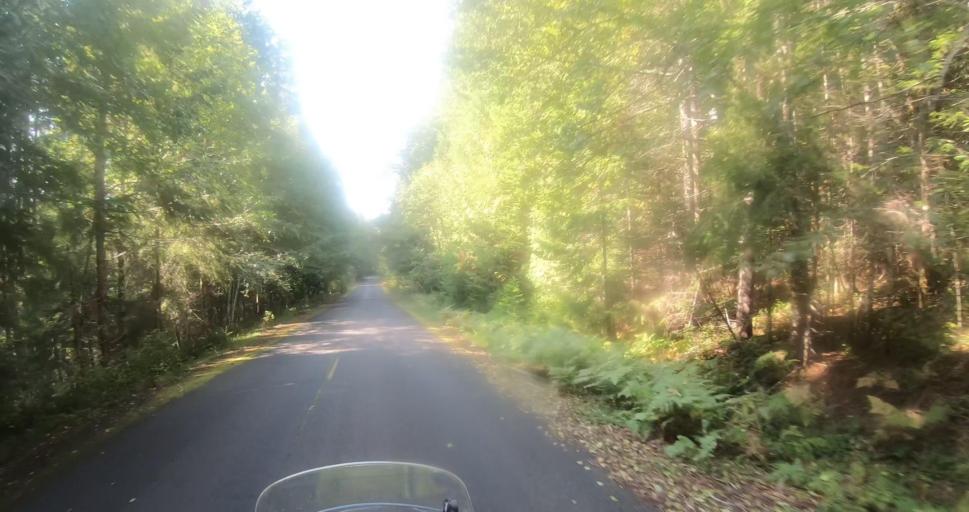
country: US
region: Washington
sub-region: Skamania County
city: Carson
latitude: 46.1846
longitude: -121.8272
